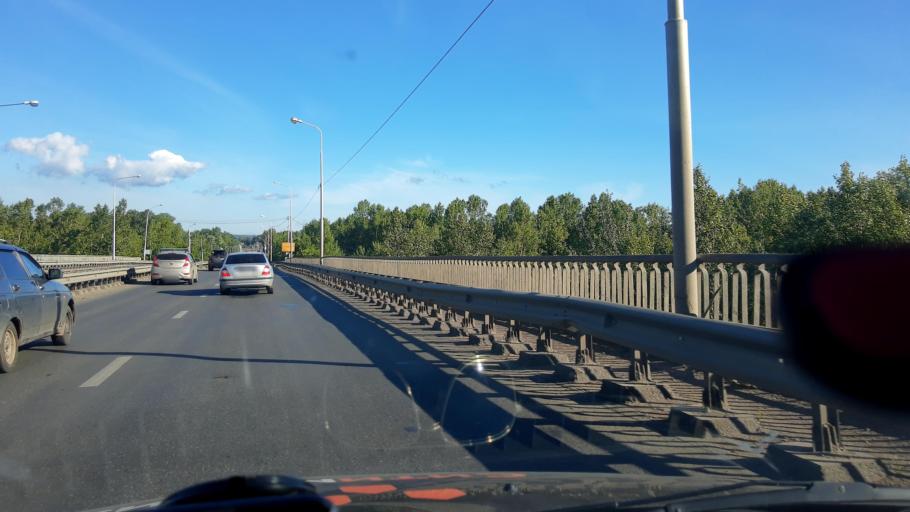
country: RU
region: Bashkortostan
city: Iglino
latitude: 54.7884
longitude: 56.2153
